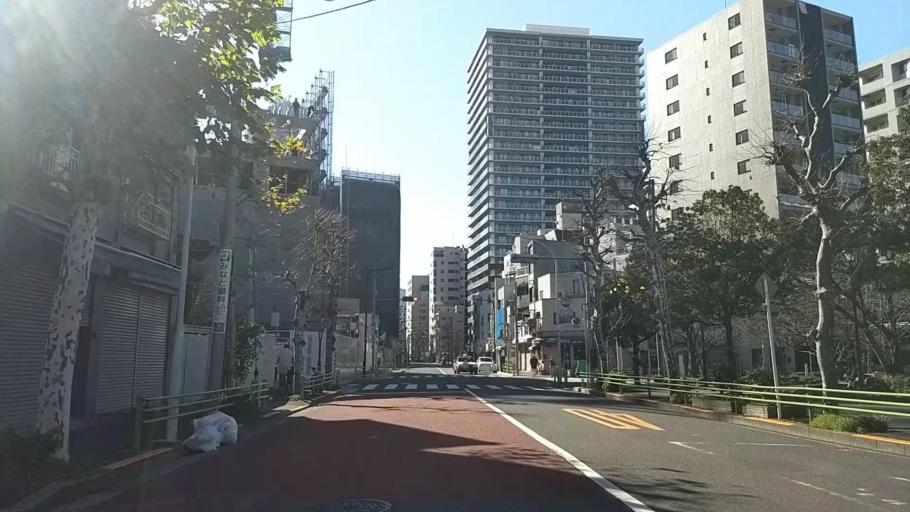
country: JP
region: Tokyo
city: Tokyo
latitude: 35.6720
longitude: 139.7800
